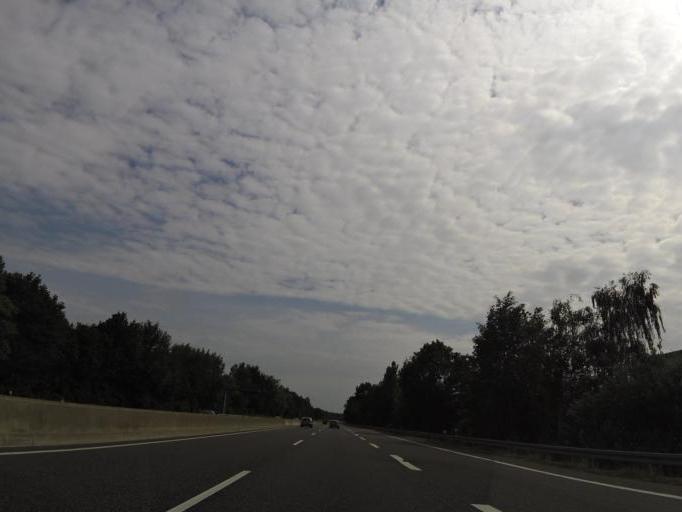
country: DE
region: Hesse
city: Dreieich
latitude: 50.0291
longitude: 8.7114
